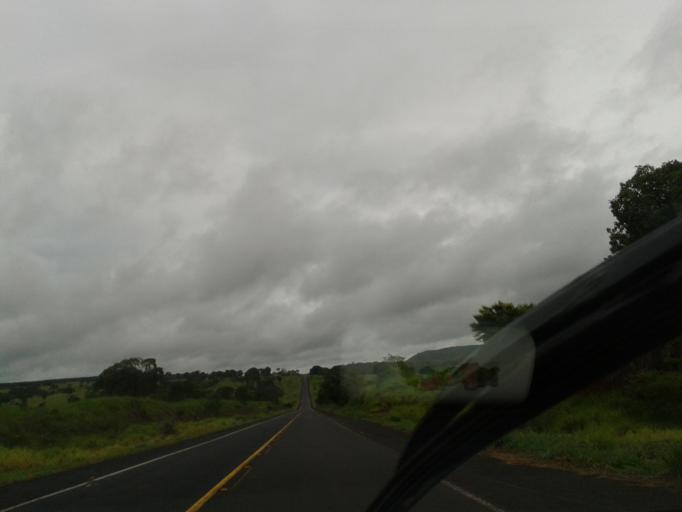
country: BR
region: Minas Gerais
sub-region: Santa Vitoria
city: Santa Vitoria
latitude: -19.2444
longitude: -50.0137
